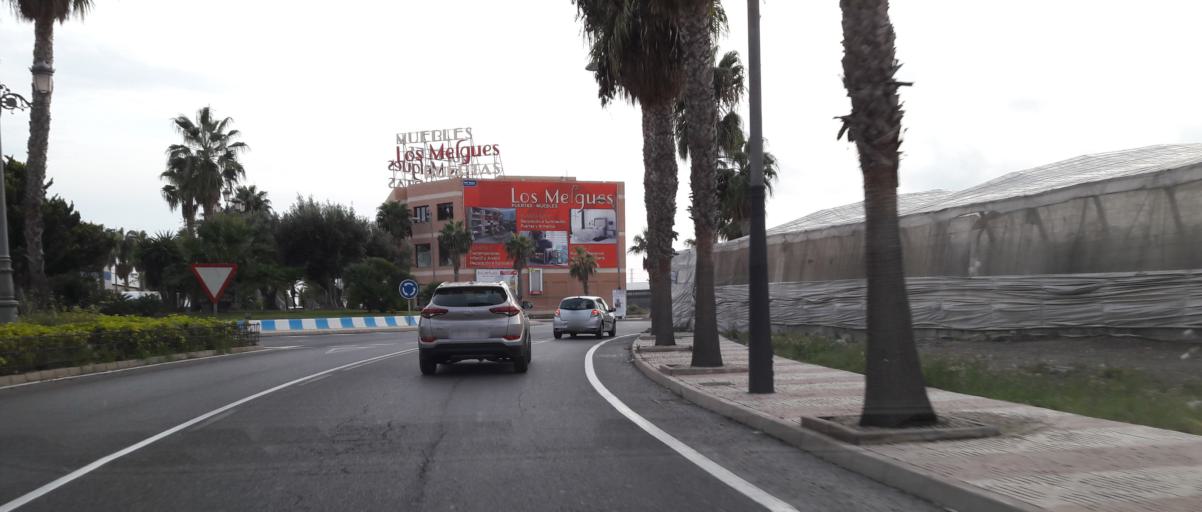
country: ES
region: Andalusia
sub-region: Provincia de Almeria
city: Roquetas de Mar
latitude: 36.7873
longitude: -2.6064
